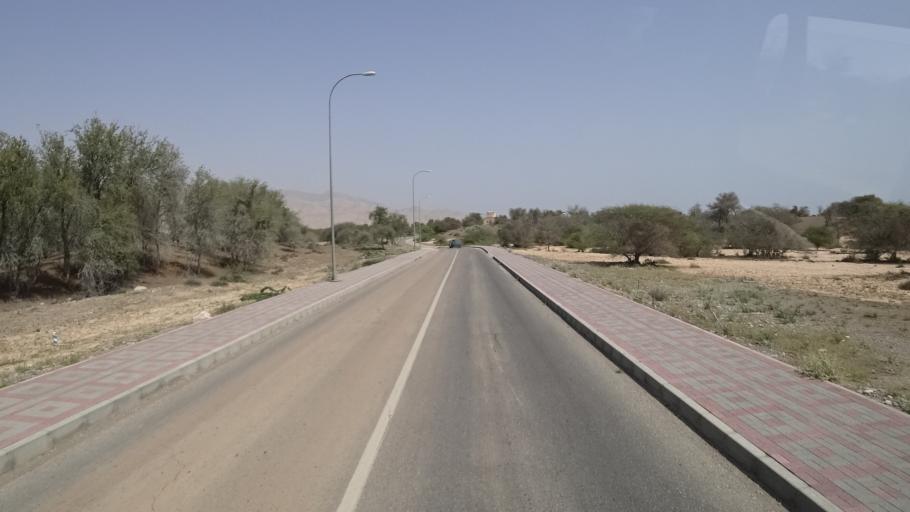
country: OM
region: Muhafazat Masqat
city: Muscat
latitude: 23.2342
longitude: 58.9107
